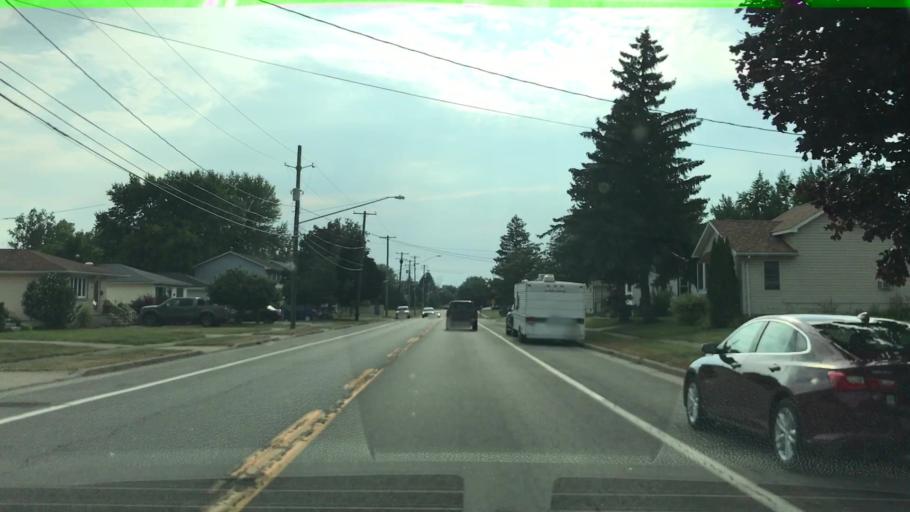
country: US
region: New York
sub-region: Erie County
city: Depew
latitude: 42.9147
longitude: -78.7044
